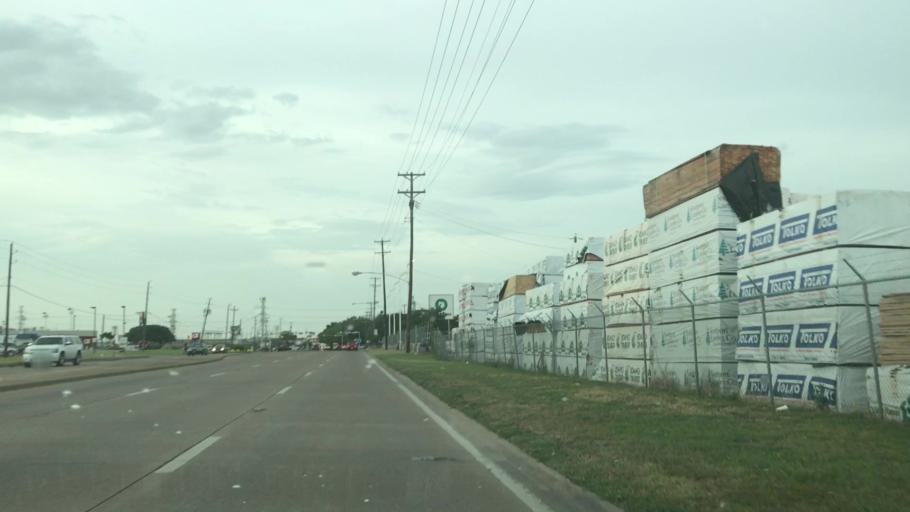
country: US
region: Texas
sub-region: Dallas County
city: Garland
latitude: 32.8615
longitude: -96.6723
